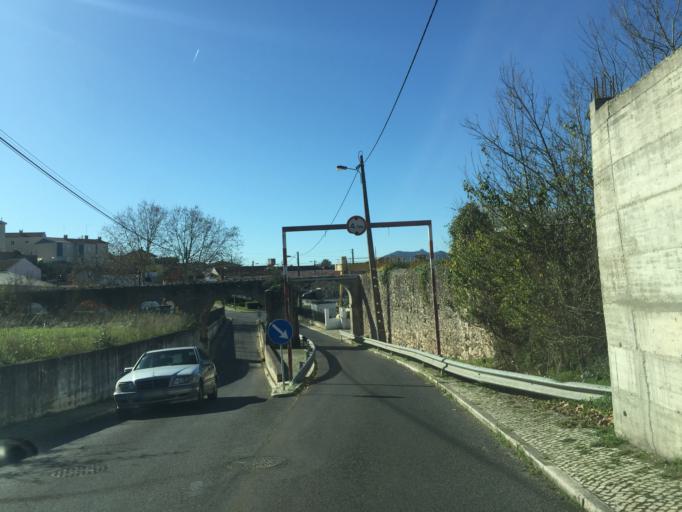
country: PT
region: Lisbon
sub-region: Sintra
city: Pero Pinheiro
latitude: 38.8474
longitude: -9.3180
